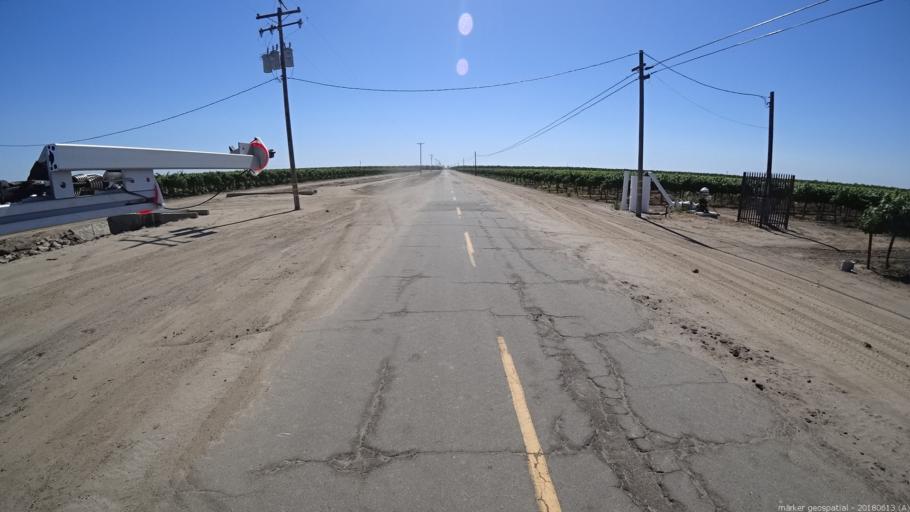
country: US
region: California
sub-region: Madera County
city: Chowchilla
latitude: 37.0689
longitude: -120.4238
